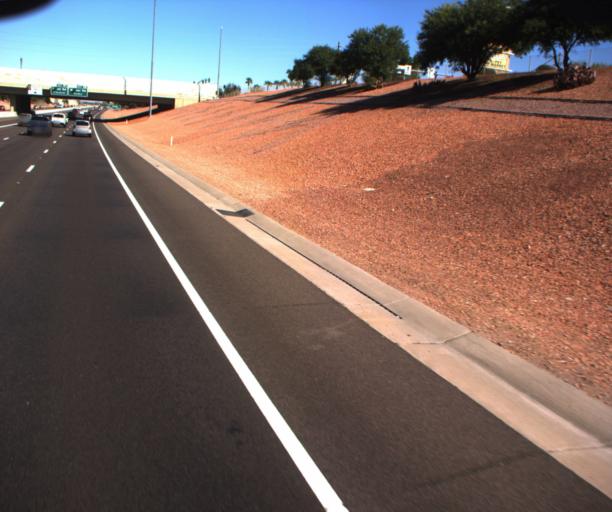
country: US
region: Arizona
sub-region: Maricopa County
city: San Carlos
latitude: 33.3188
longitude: -111.8941
